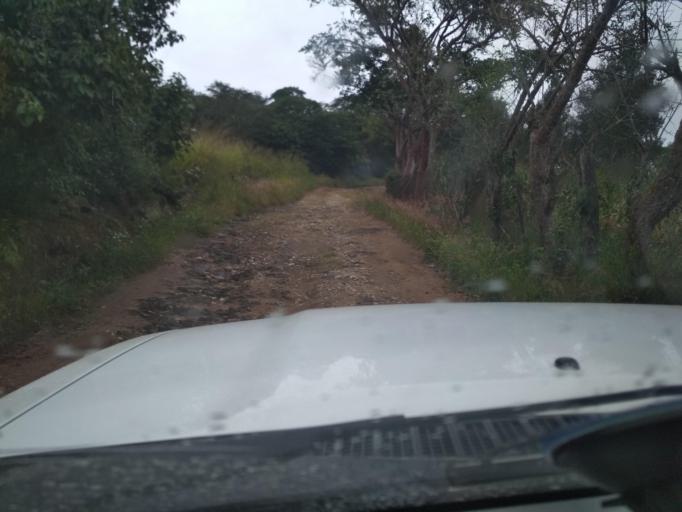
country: MX
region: Veracruz
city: El Castillo
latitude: 19.5364
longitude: -96.8257
